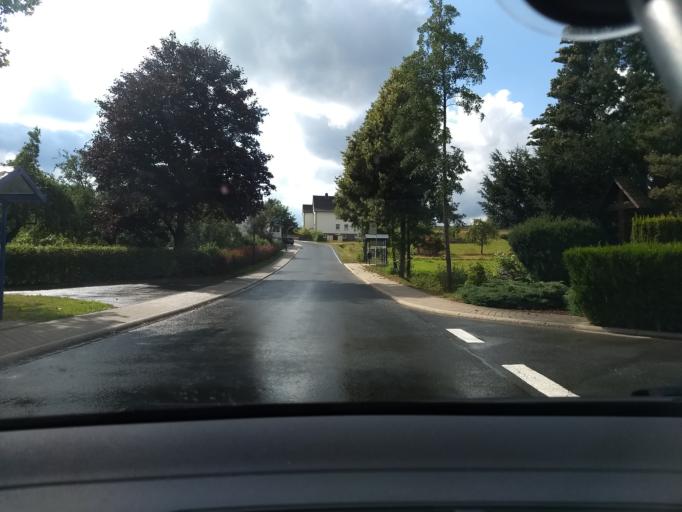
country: DE
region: North Rhine-Westphalia
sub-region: Regierungsbezirk Arnsberg
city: Finnentrop
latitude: 51.1911
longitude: 8.0140
